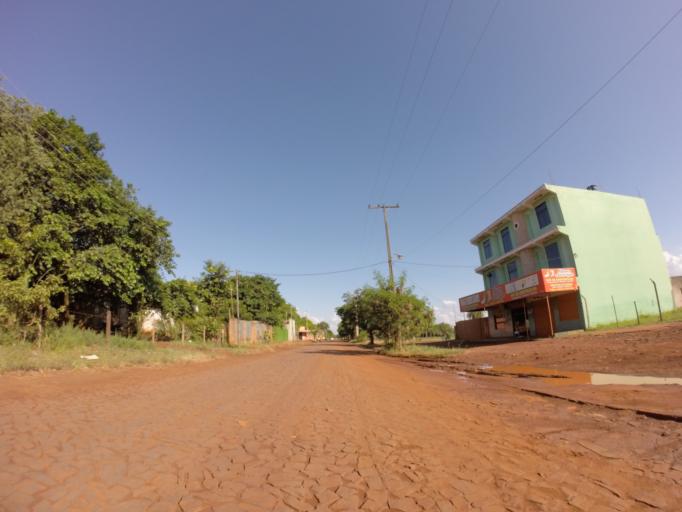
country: PY
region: Alto Parana
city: Ciudad del Este
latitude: -25.3873
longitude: -54.6537
